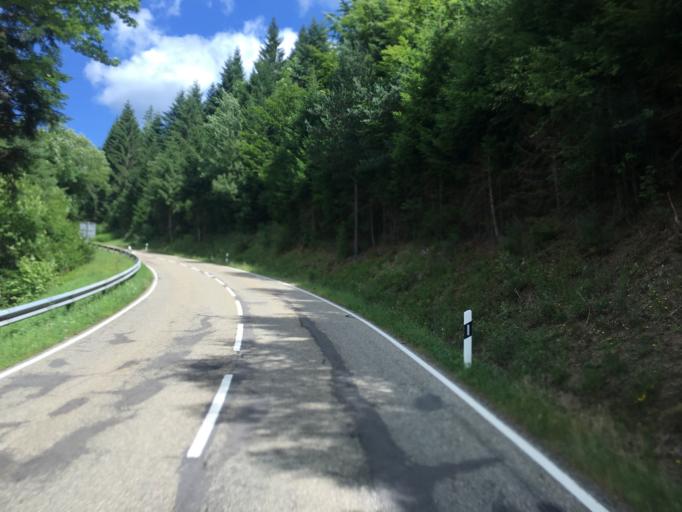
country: DE
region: Baden-Wuerttemberg
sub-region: Karlsruhe Region
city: Forbach
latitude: 48.6402
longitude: 8.3397
